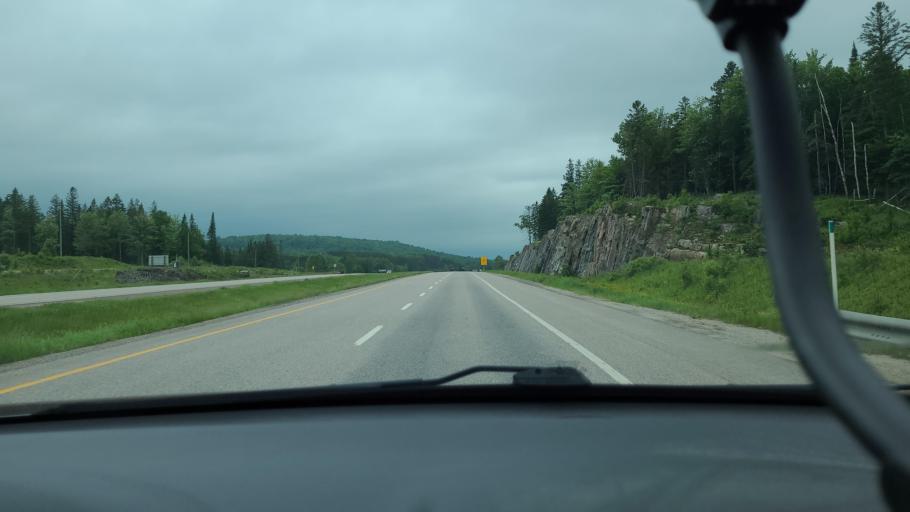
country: CA
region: Quebec
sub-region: Laurentides
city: Labelle
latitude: 46.2820
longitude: -74.7565
